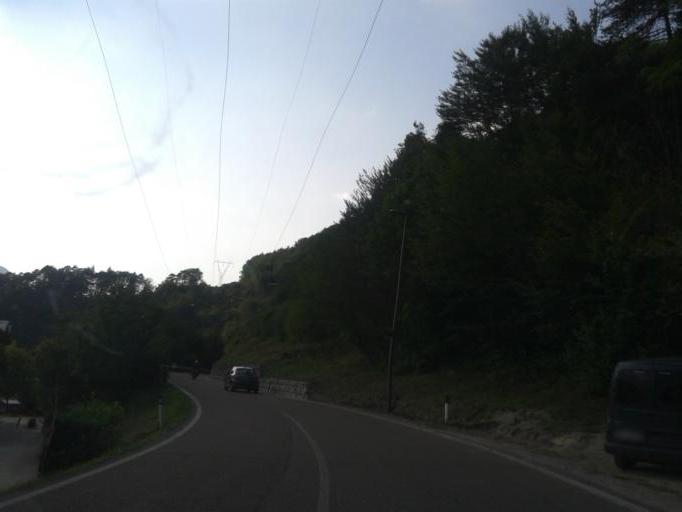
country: IT
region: Trentino-Alto Adige
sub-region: Provincia di Trento
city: Molina di Ledro
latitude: 45.8781
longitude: 10.7683
